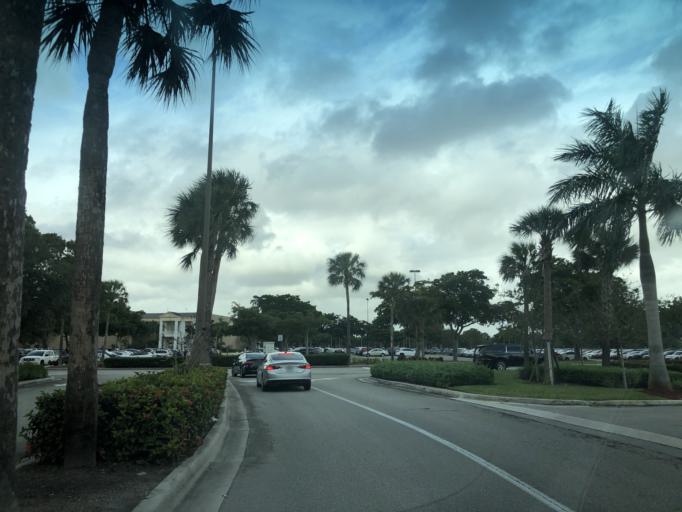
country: US
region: Florida
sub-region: Broward County
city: Tamarac
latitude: 26.2388
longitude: -80.2468
